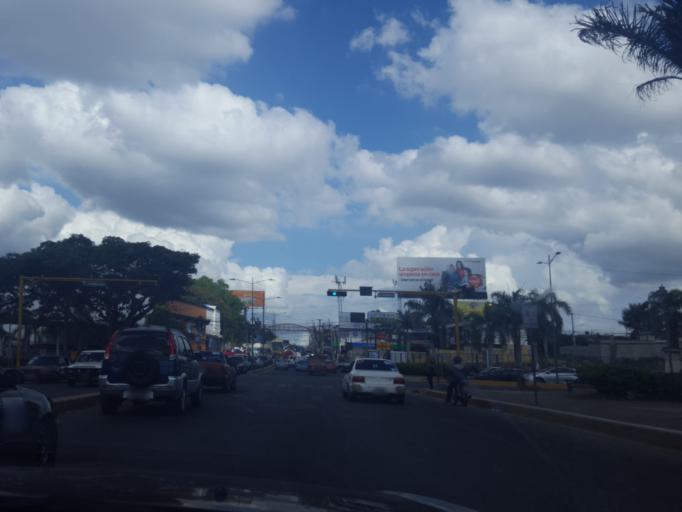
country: DO
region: Santiago
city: Santiago de los Caballeros
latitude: 19.4319
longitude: -70.6934
